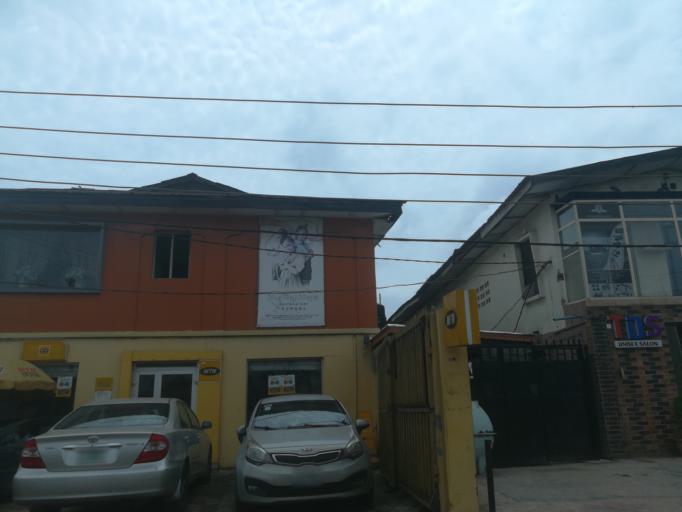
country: NG
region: Lagos
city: Somolu
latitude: 6.5289
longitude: 3.3871
